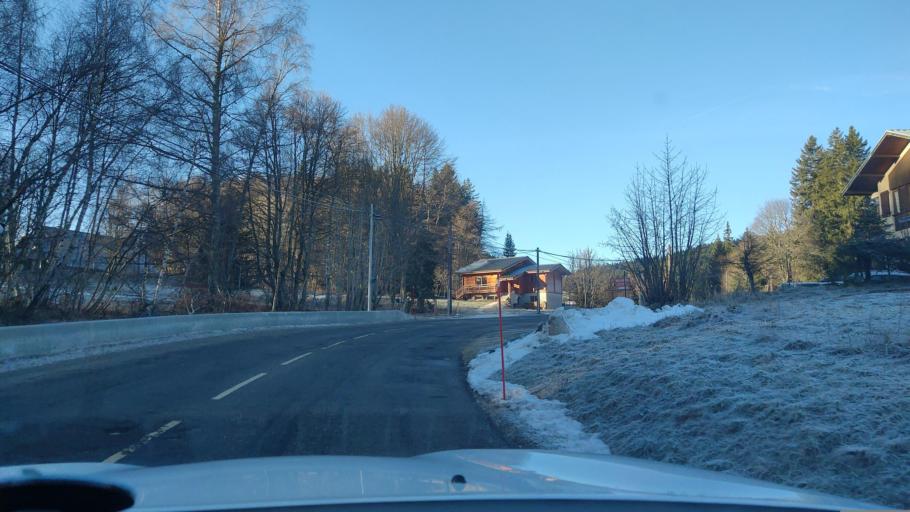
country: FR
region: Rhone-Alpes
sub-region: Departement de la Savoie
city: Mery
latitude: 45.6423
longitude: 5.9943
